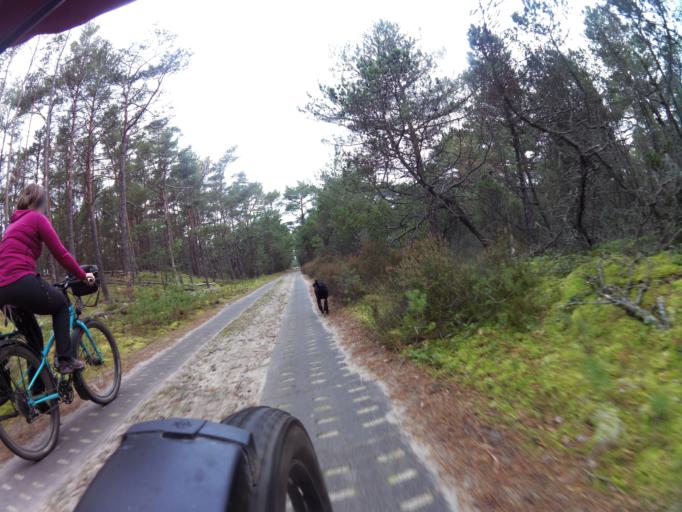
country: PL
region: Pomeranian Voivodeship
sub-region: Powiat pucki
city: Hel
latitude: 54.6256
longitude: 18.8159
